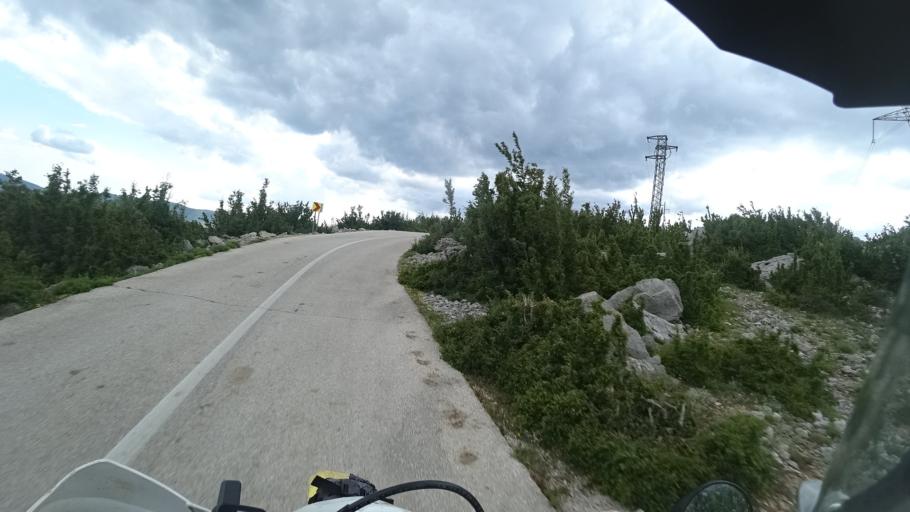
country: HR
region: Zadarska
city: Gracac
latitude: 44.2036
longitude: 15.8550
